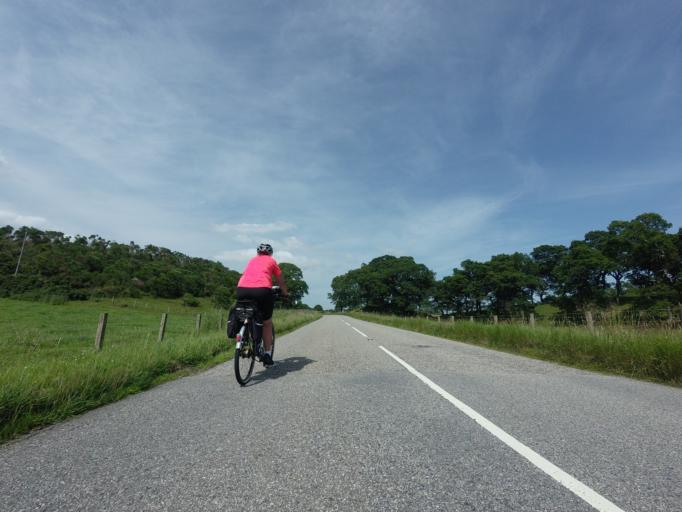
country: GB
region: Scotland
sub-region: Highland
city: Tain
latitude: 57.8504
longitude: -4.2036
